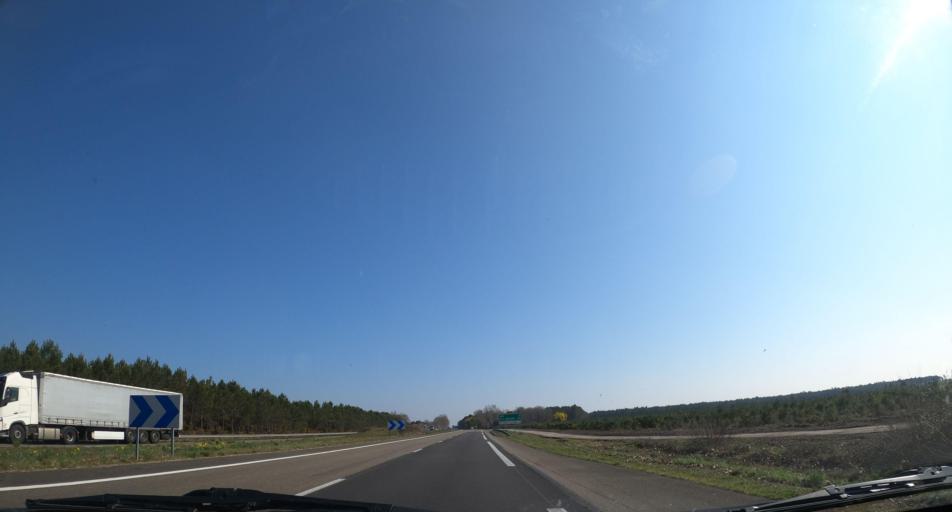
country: FR
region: Aquitaine
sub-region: Departement des Landes
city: Riviere-Saas-et-Gourby
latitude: 43.7095
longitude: -1.1585
